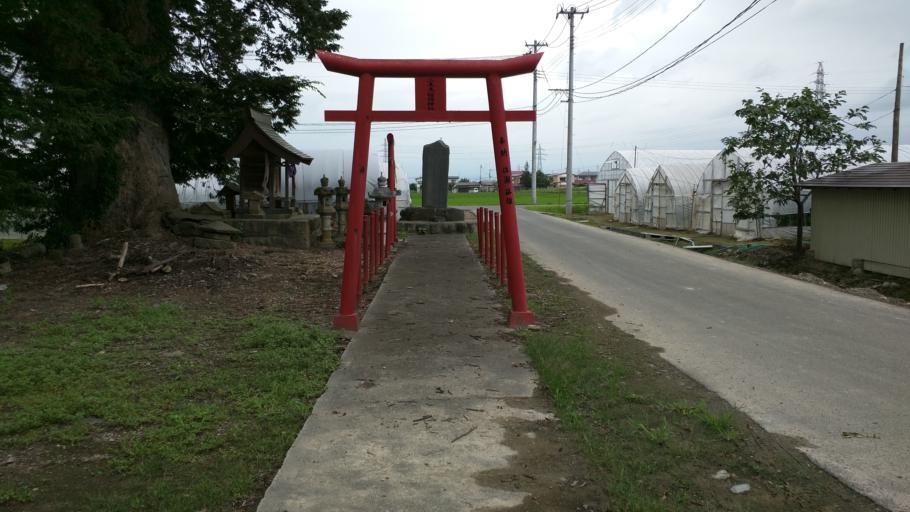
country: JP
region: Fukushima
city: Kitakata
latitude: 37.4898
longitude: 139.9009
